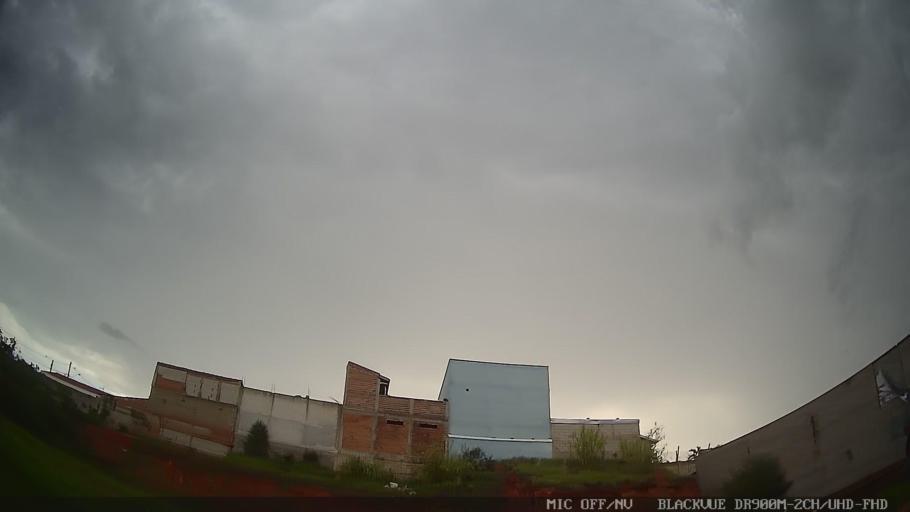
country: BR
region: Sao Paulo
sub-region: Pedreira
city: Pedreira
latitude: -22.7046
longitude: -46.8968
